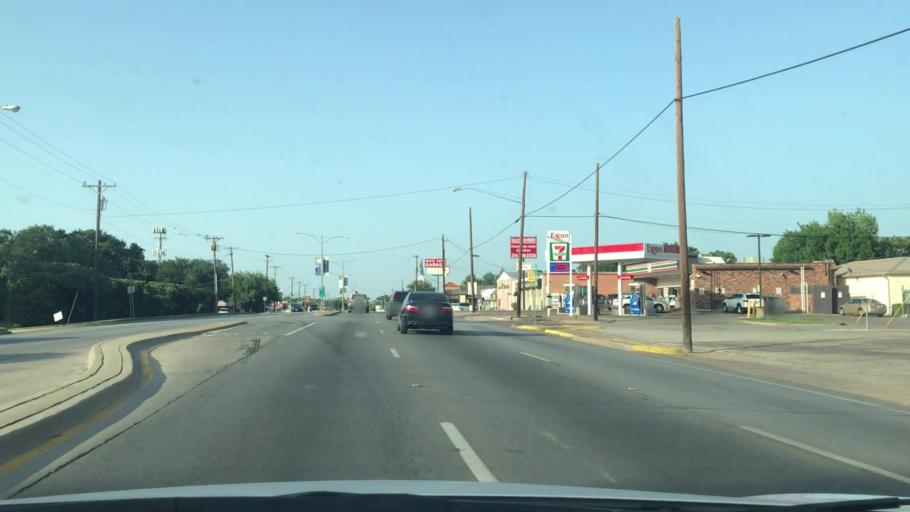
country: US
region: Texas
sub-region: Dallas County
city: Highland Park
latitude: 32.8258
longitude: -96.7117
